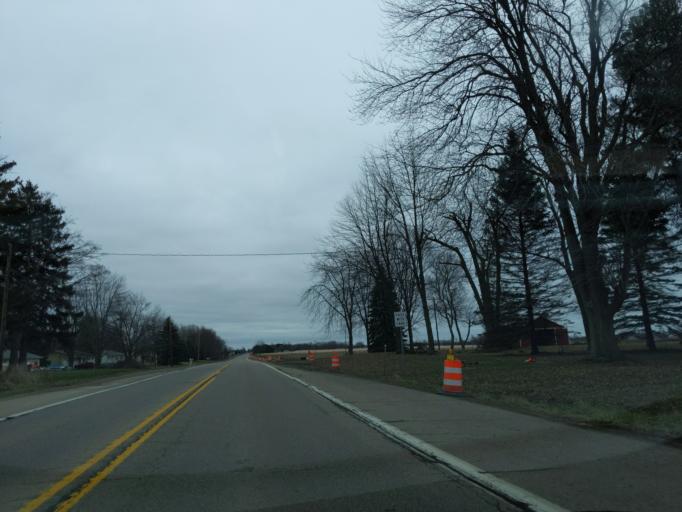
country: US
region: Michigan
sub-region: Clinton County
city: Saint Johns
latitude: 43.0013
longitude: -84.5104
